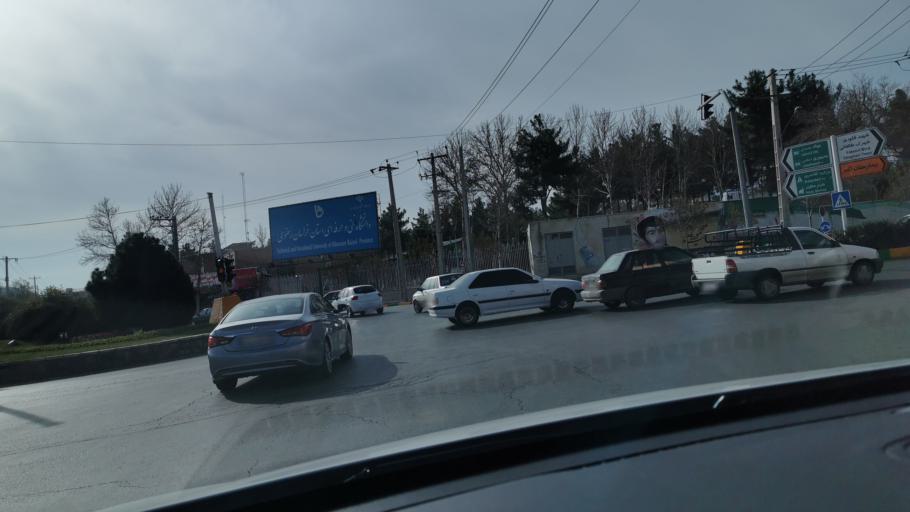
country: IR
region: Razavi Khorasan
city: Mashhad
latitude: 36.2844
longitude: 59.5485
